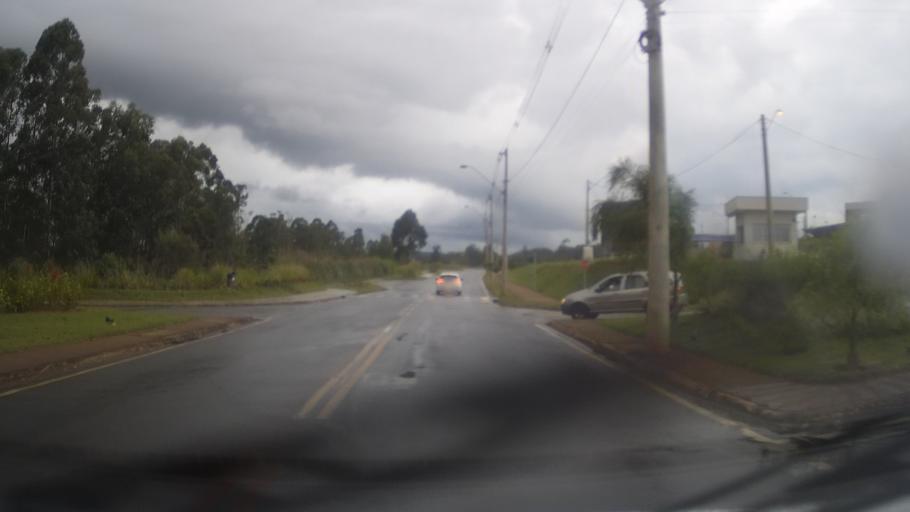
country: BR
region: Sao Paulo
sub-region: Itupeva
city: Itupeva
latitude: -23.1799
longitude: -47.0478
